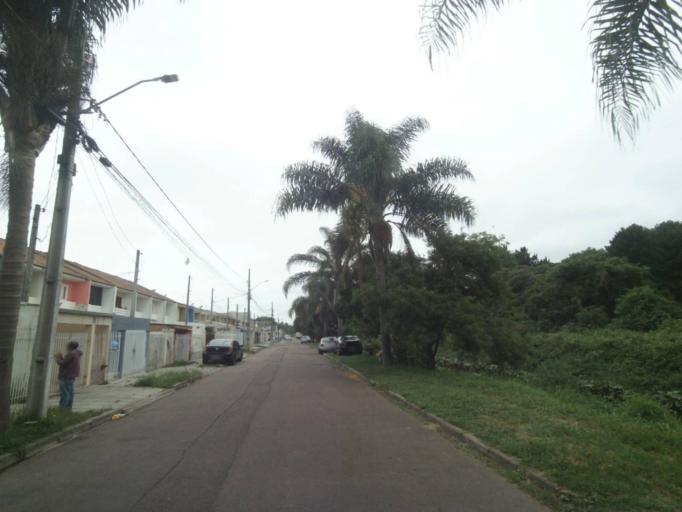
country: BR
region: Parana
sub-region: Araucaria
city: Araucaria
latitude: -25.5487
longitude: -49.3440
